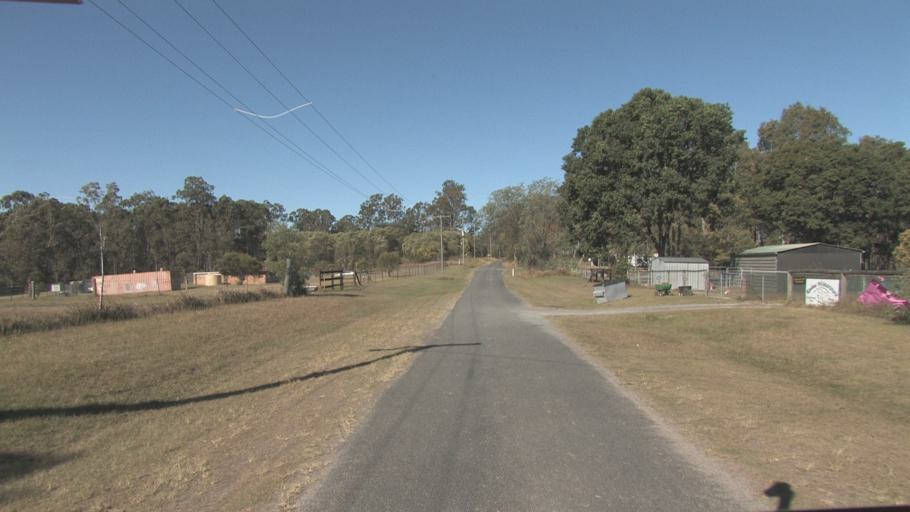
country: AU
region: Queensland
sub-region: Ipswich
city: Springfield Lakes
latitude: -27.7262
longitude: 152.9502
